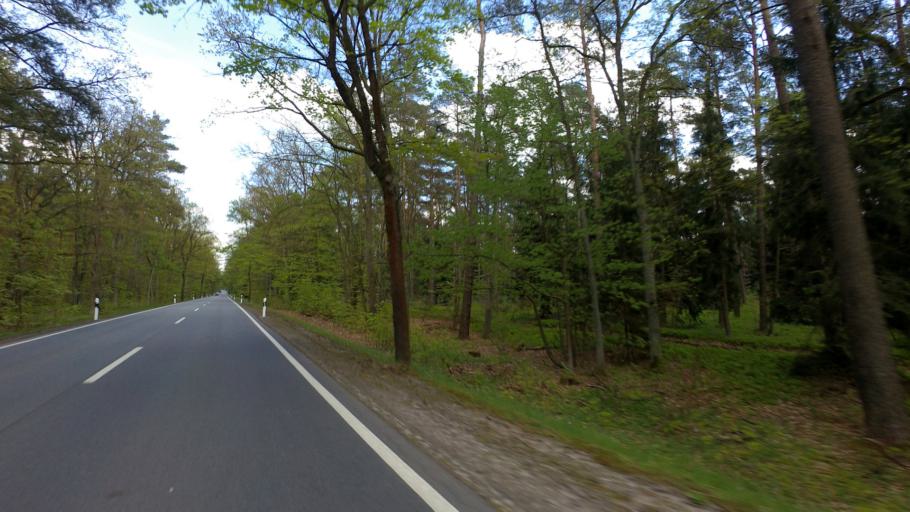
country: DE
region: Brandenburg
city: Marienwerder
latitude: 52.8402
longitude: 13.5124
